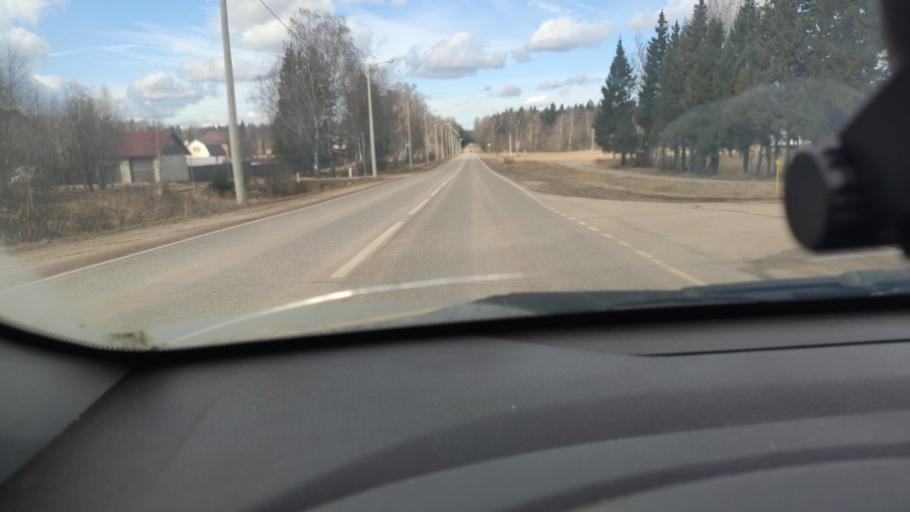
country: RU
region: Moskovskaya
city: Ruza
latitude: 55.7147
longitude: 36.1726
